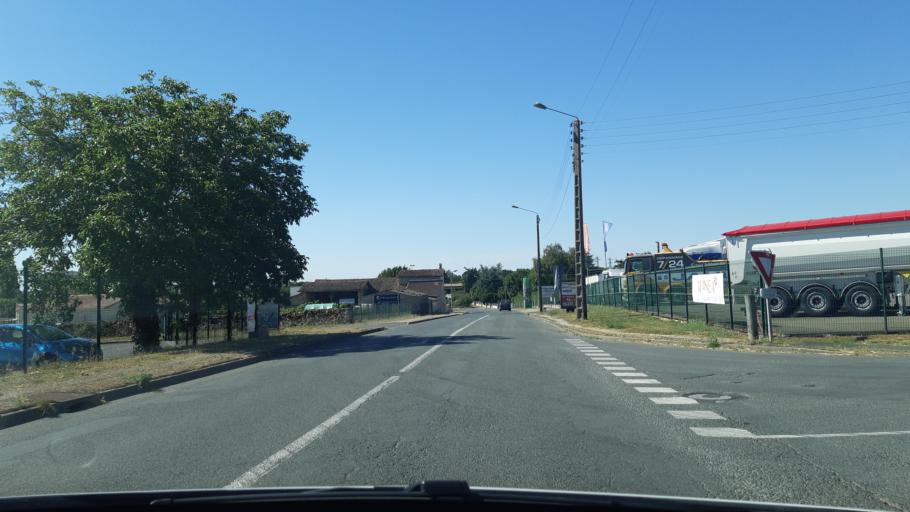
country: FR
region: Poitou-Charentes
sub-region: Departement des Deux-Sevres
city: Exireuil
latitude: 46.4223
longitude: -0.2063
